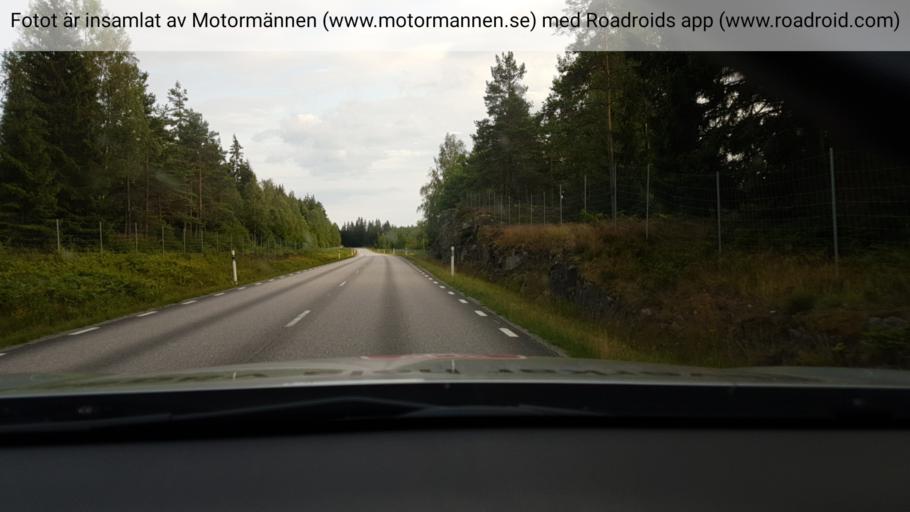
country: SE
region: Vaestra Goetaland
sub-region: Fargelanda Kommun
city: Faergelanda
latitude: 58.4816
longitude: 12.0081
